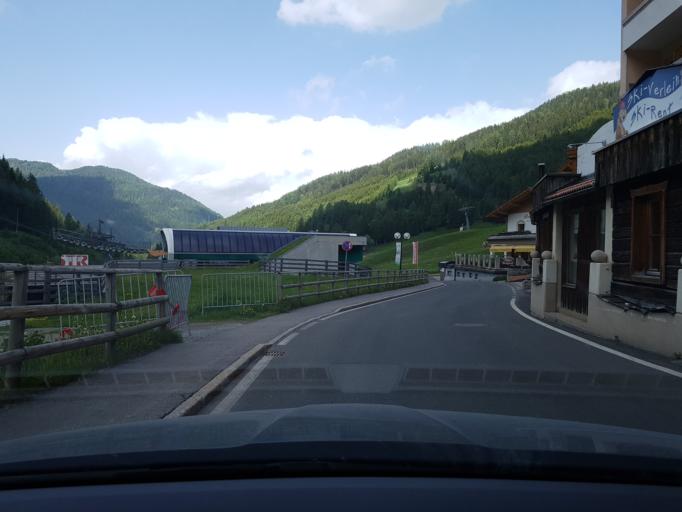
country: AT
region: Salzburg
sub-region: Politischer Bezirk Tamsweg
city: Thomatal
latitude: 46.9711
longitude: 13.7494
